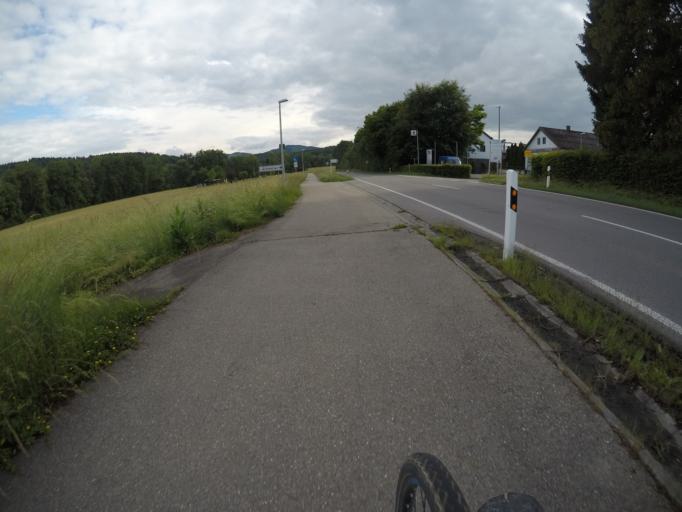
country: DE
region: Baden-Wuerttemberg
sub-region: Regierungsbezirk Stuttgart
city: Frickenhausen
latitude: 48.5888
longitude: 9.3473
